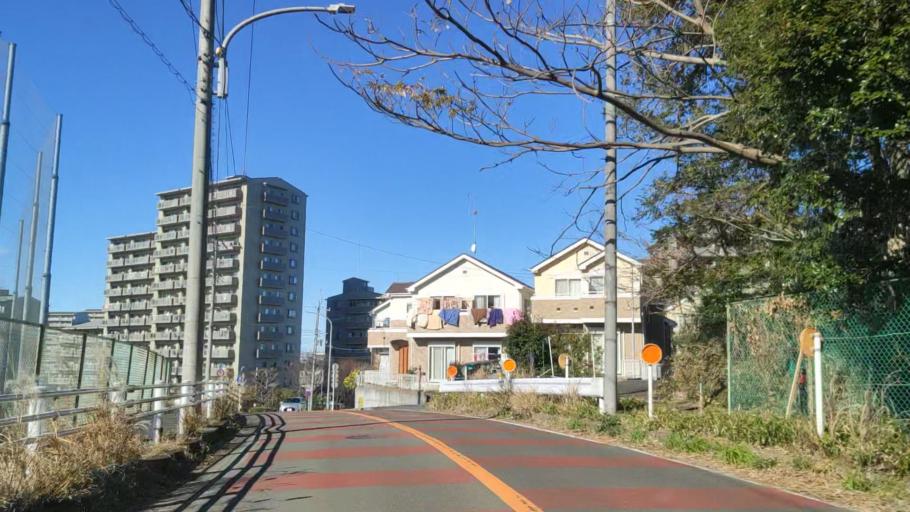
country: JP
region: Kanagawa
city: Minami-rinkan
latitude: 35.5061
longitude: 139.5347
